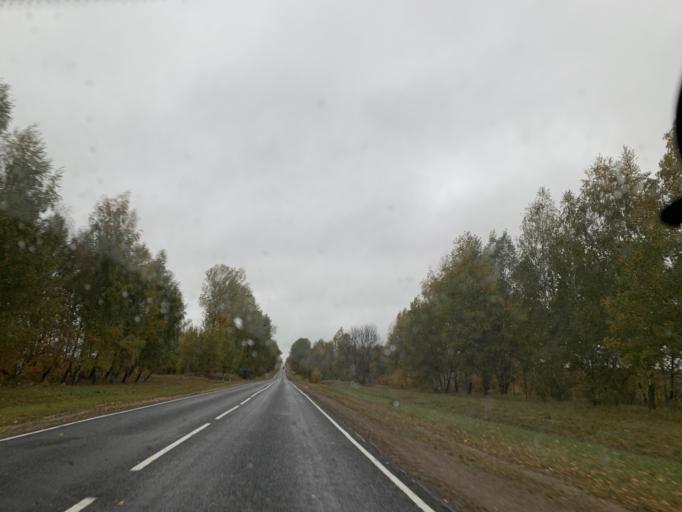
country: BY
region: Minsk
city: Novy Svyerzhan'
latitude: 53.4274
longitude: 26.6373
